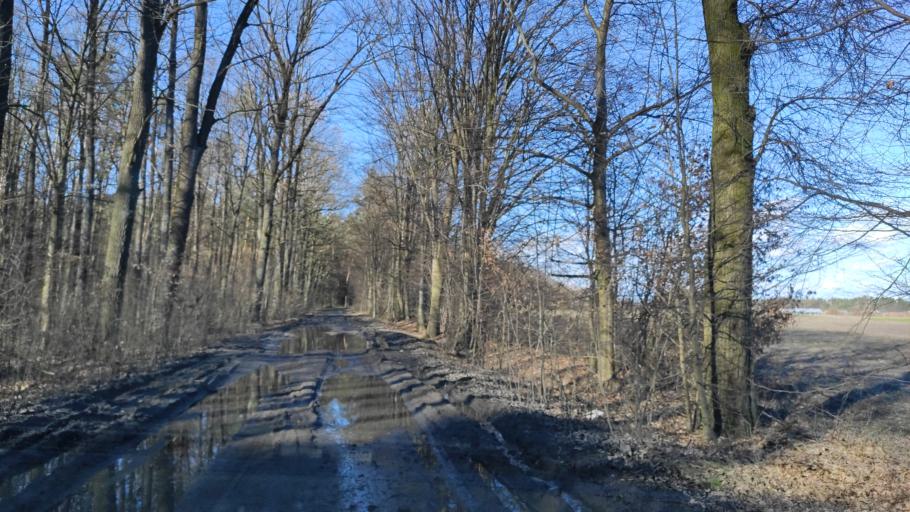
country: PL
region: Masovian Voivodeship
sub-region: Powiat radomski
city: Jedlnia-Letnisko
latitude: 51.4564
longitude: 21.3244
